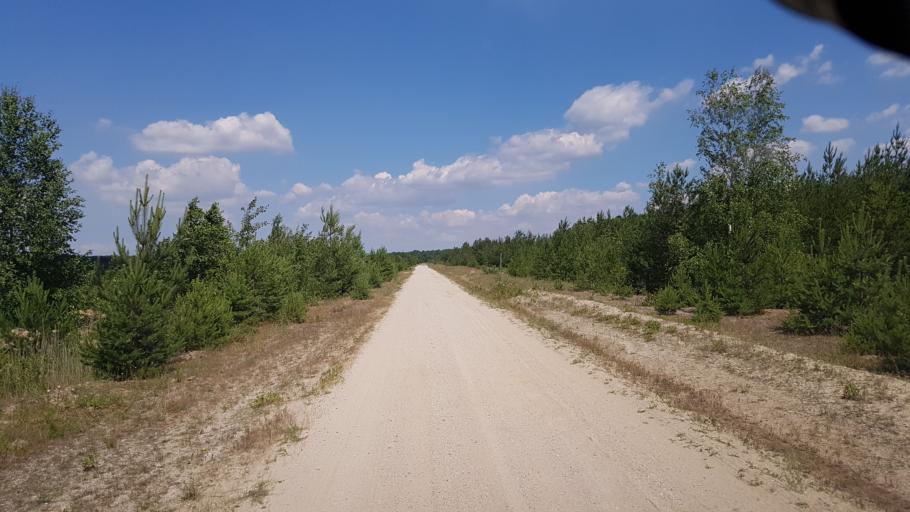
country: DE
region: Brandenburg
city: Sallgast
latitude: 51.5800
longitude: 13.8004
